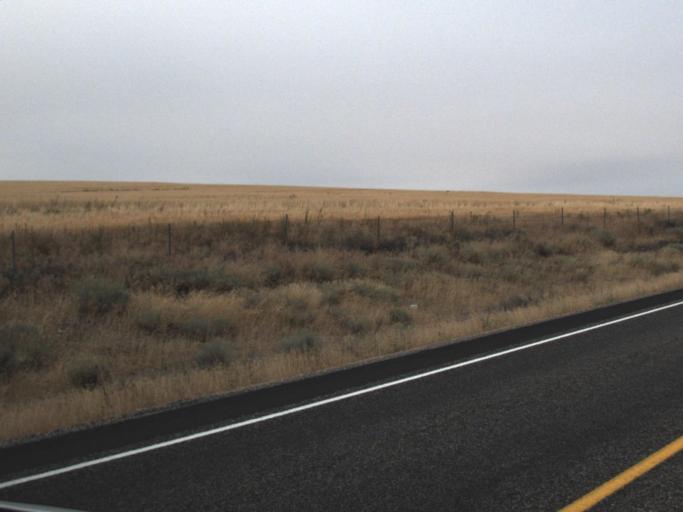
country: US
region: Washington
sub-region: Benton County
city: Prosser
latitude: 46.1927
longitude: -119.7059
